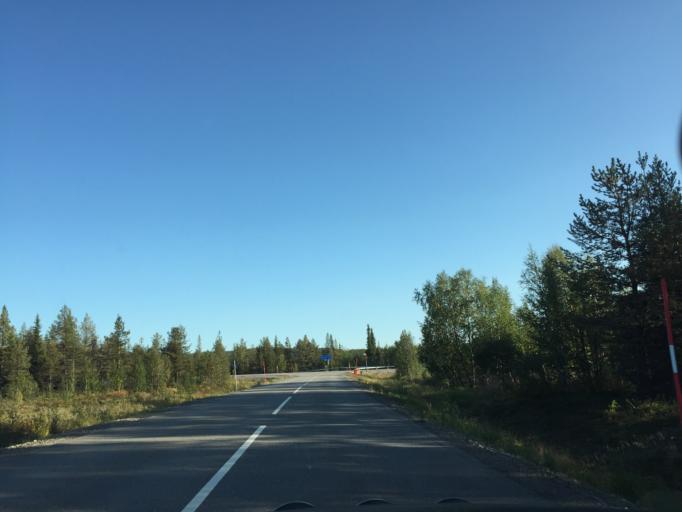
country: SE
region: Norrbotten
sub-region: Gallivare Kommun
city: Malmberget
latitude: 67.6375
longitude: 21.0719
